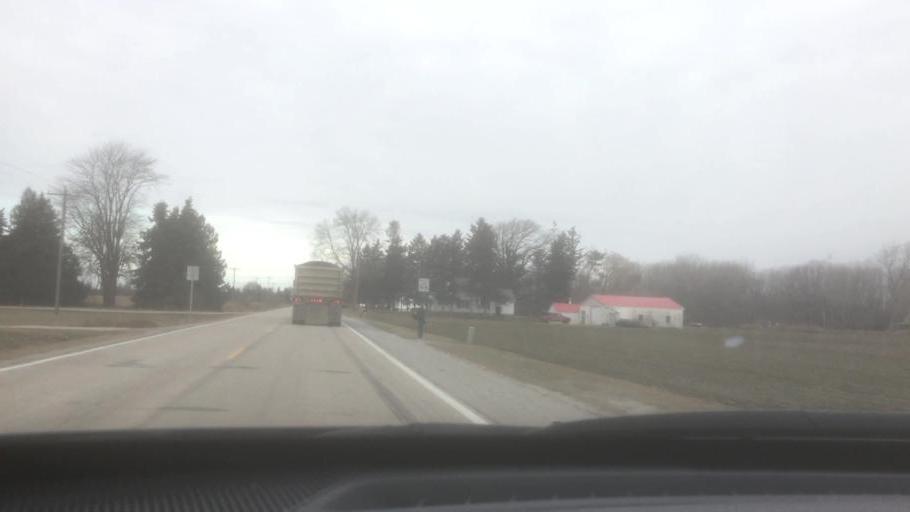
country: US
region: Michigan
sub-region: Bay County
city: Essexville
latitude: 43.5221
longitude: -83.7848
